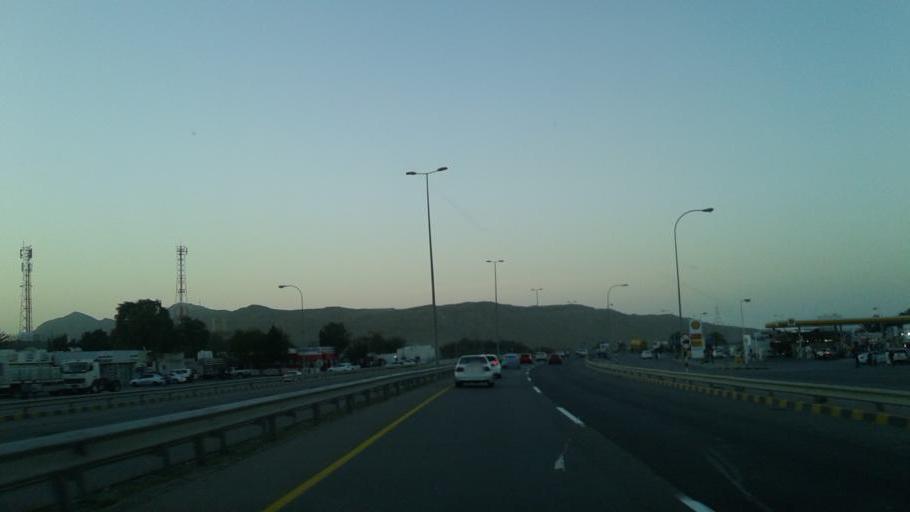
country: OM
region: Muhafazat ad Dakhiliyah
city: Bidbid
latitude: 23.5255
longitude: 58.1893
